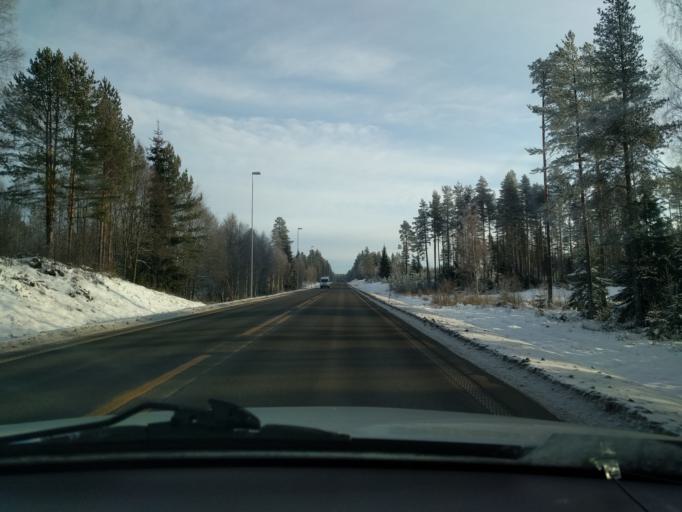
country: NO
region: Hedmark
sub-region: Elverum
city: Elverum
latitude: 60.9073
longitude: 11.6183
